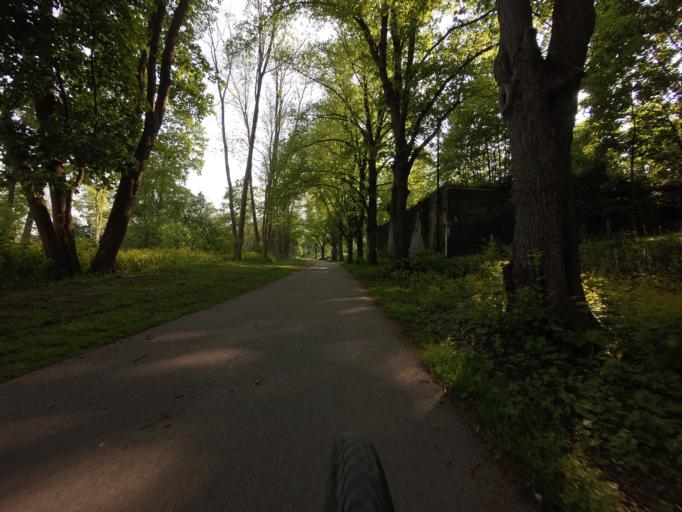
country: DK
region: Capital Region
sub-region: Rodovre Kommune
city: Rodovre
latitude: 55.6896
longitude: 12.4372
